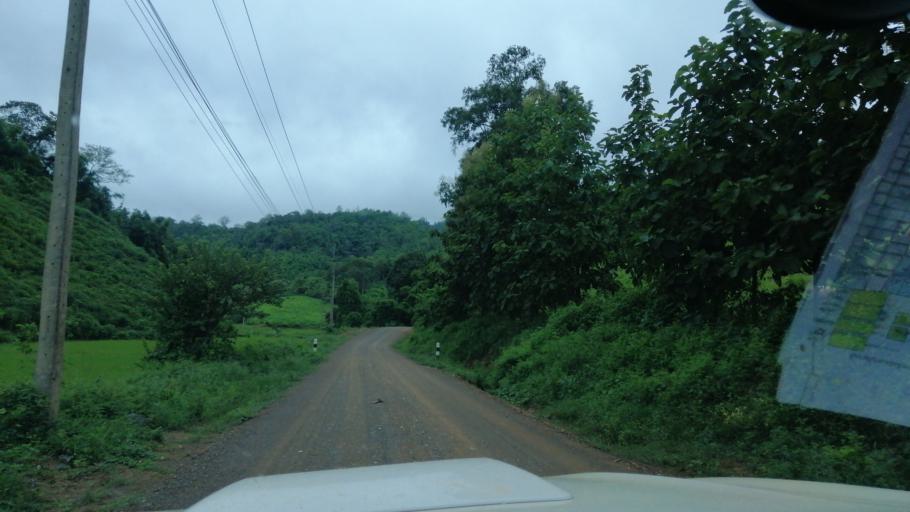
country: LA
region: Xiagnabouli
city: Muang Kenthao
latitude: 17.9432
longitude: 101.3968
